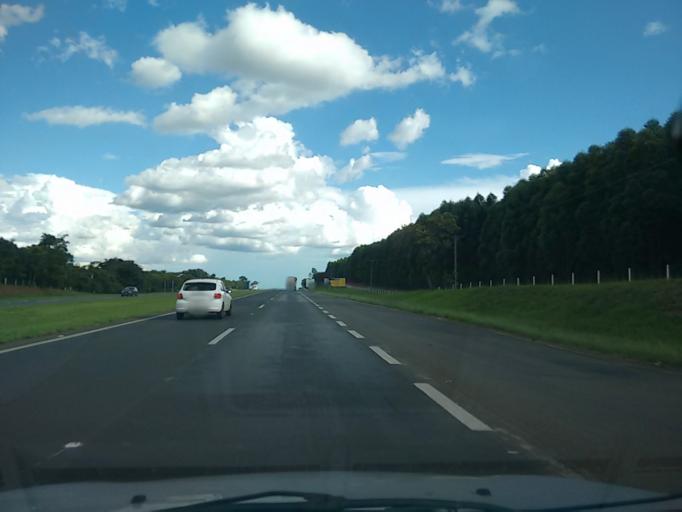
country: BR
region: Sao Paulo
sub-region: Sao Carlos
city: Sao Carlos
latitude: -22.0479
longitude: -47.8602
